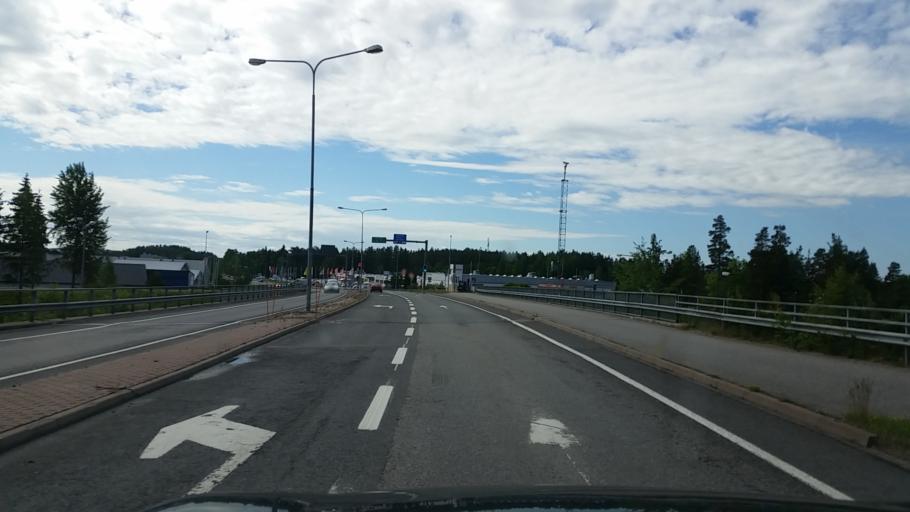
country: FI
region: Varsinais-Suomi
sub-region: Turku
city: Kaarina
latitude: 60.4242
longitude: 22.3796
